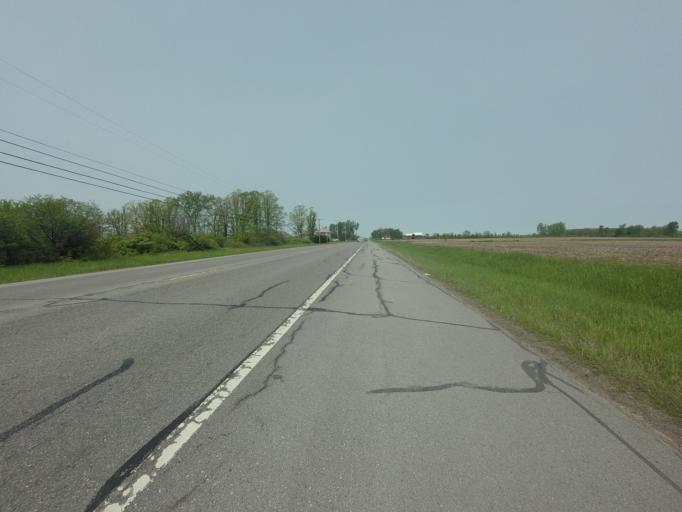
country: US
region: New York
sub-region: Jefferson County
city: Dexter
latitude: 44.0359
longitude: -76.0650
